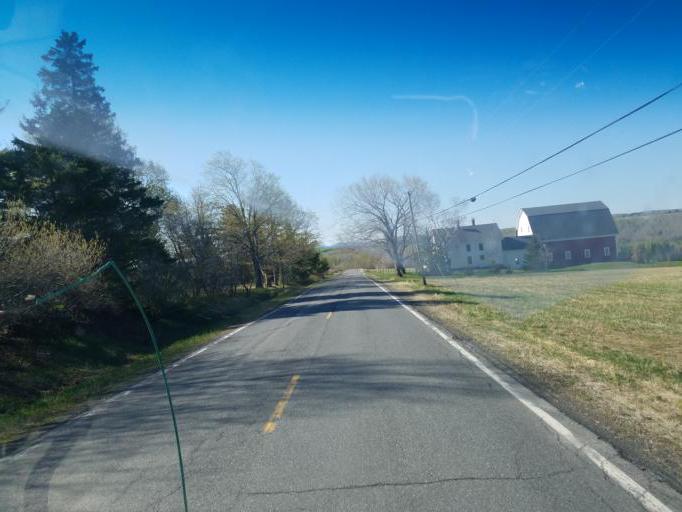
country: US
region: Maine
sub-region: Aroostook County
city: Caribou
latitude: 46.8641
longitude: -68.2087
